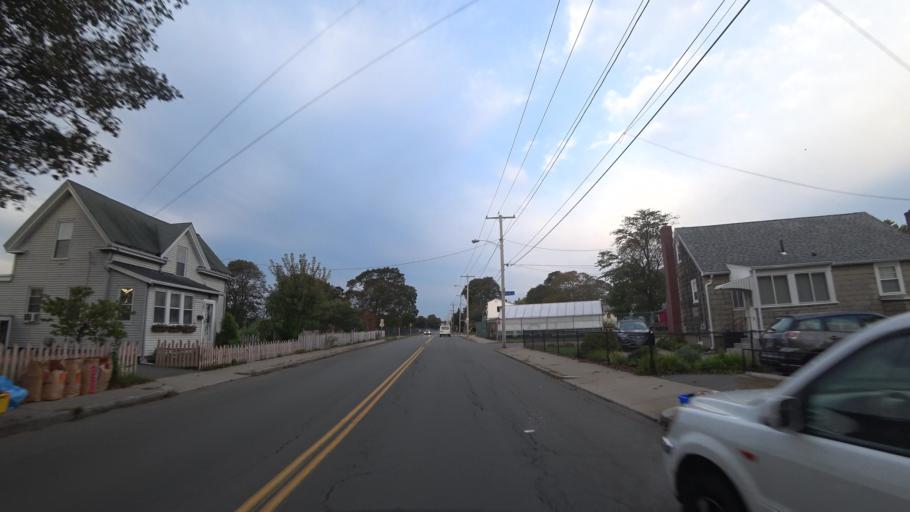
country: US
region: Massachusetts
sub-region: Suffolk County
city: Revere
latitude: 42.4296
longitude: -71.0306
